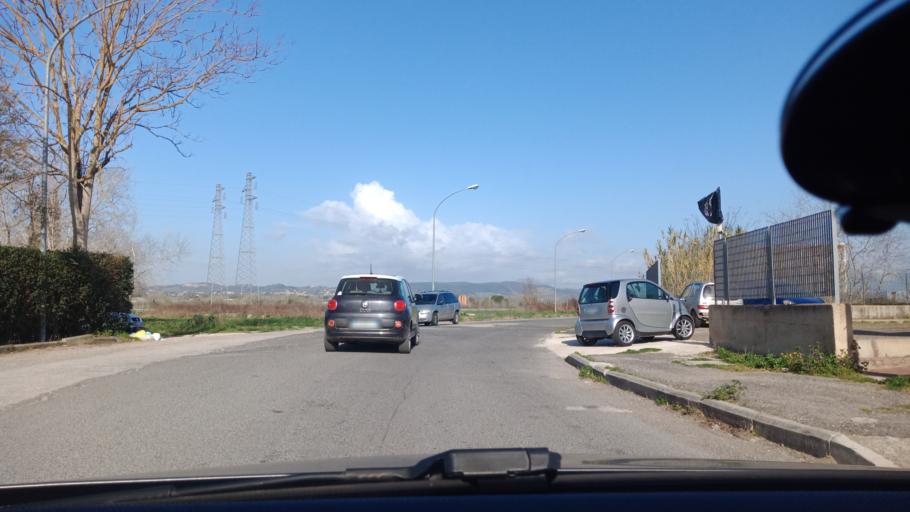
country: IT
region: Latium
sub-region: Citta metropolitana di Roma Capitale
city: Fiano Romano
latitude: 42.1536
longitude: 12.6465
